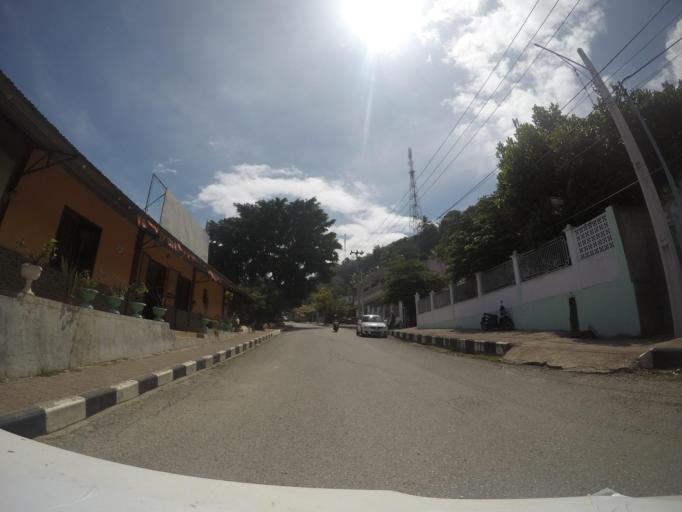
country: TL
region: Baucau
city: Baucau
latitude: -8.4634
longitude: 126.4538
